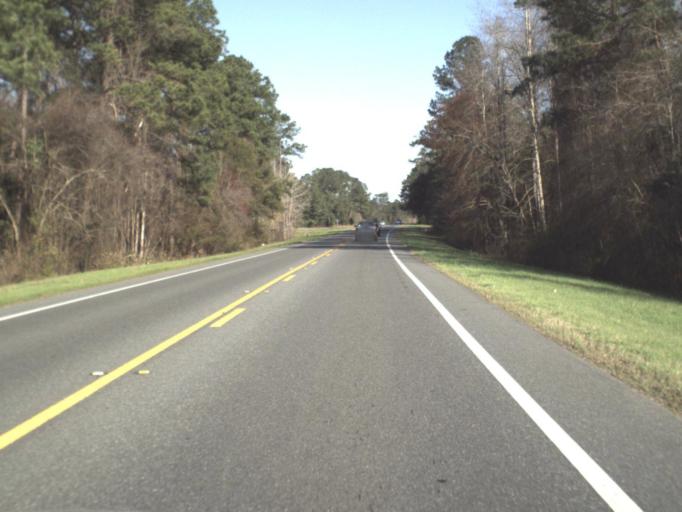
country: US
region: Florida
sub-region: Jackson County
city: Marianna
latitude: 30.7457
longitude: -85.1691
